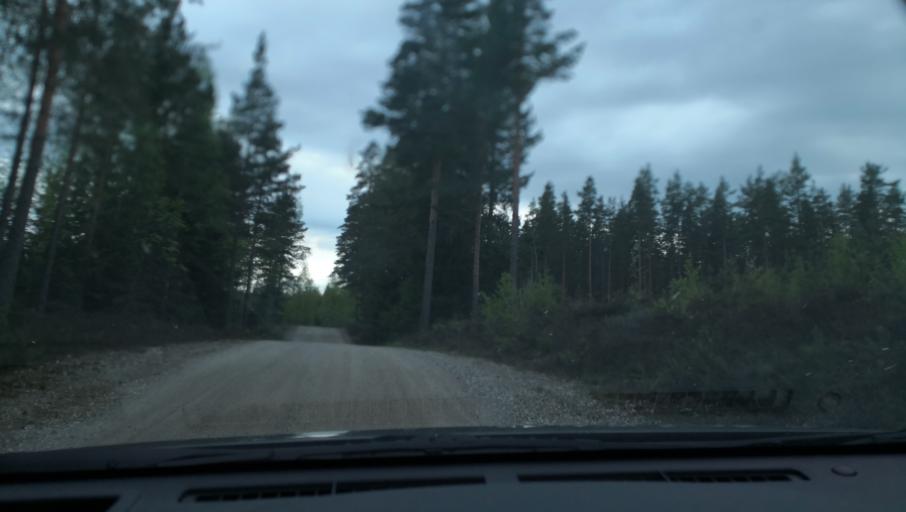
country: SE
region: Vaestmanland
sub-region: Skinnskattebergs Kommun
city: Skinnskatteberg
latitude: 59.8068
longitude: 15.5163
